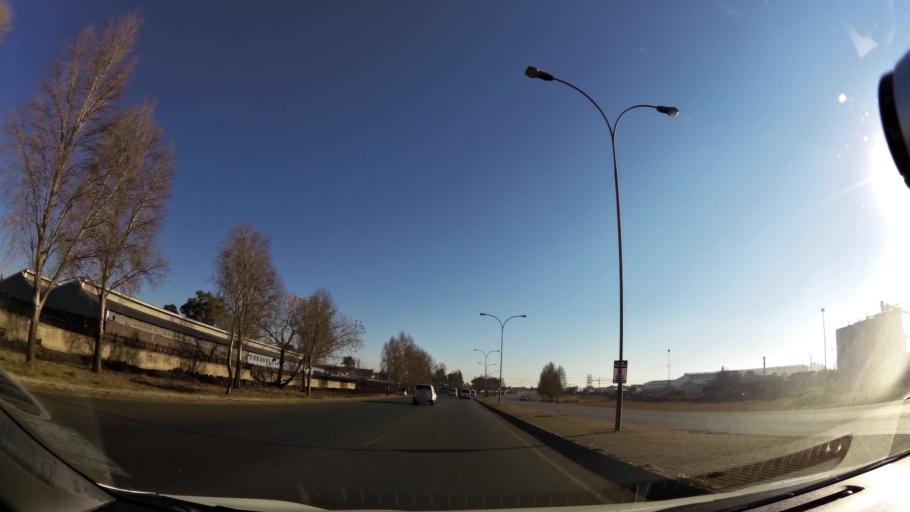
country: ZA
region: Gauteng
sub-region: Ekurhuleni Metropolitan Municipality
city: Germiston
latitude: -26.3059
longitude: 28.1378
